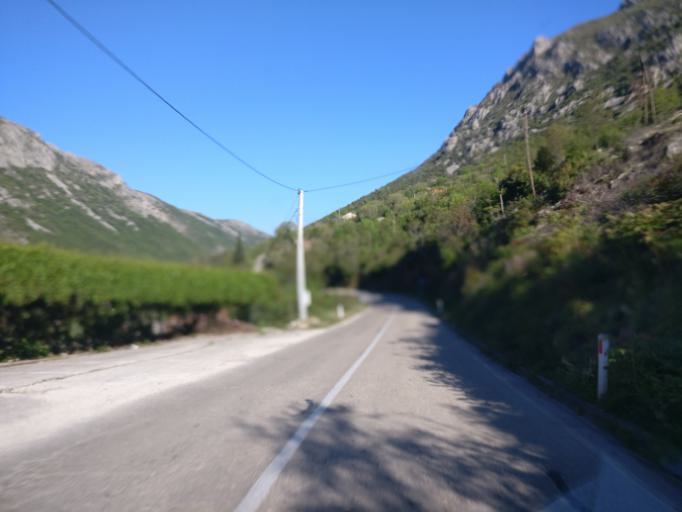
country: BA
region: Federation of Bosnia and Herzegovina
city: Stolac
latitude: 43.0773
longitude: 18.0229
